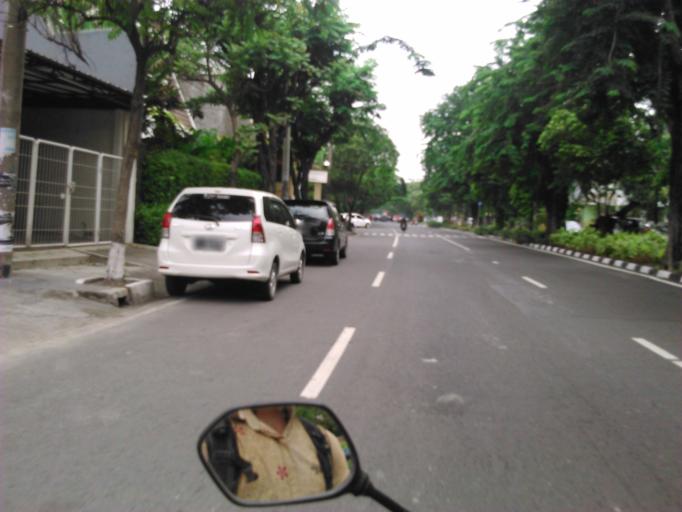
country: ID
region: East Java
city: Pacarkeling
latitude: -7.2596
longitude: 112.7511
